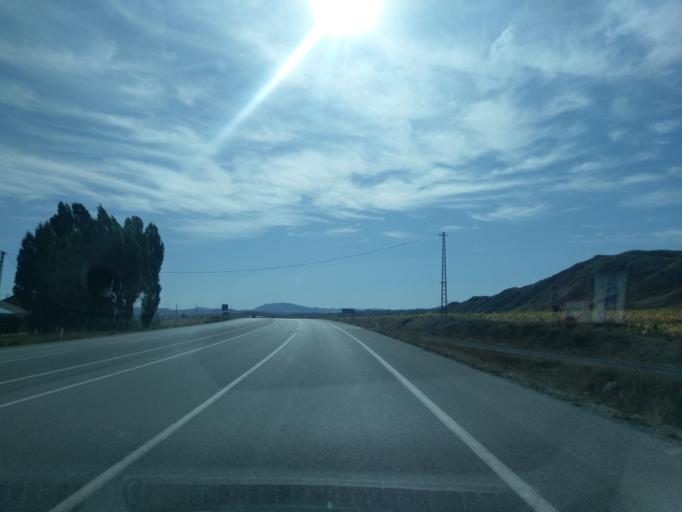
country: TR
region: Sivas
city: Imranli
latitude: 39.8792
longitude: 38.0711
